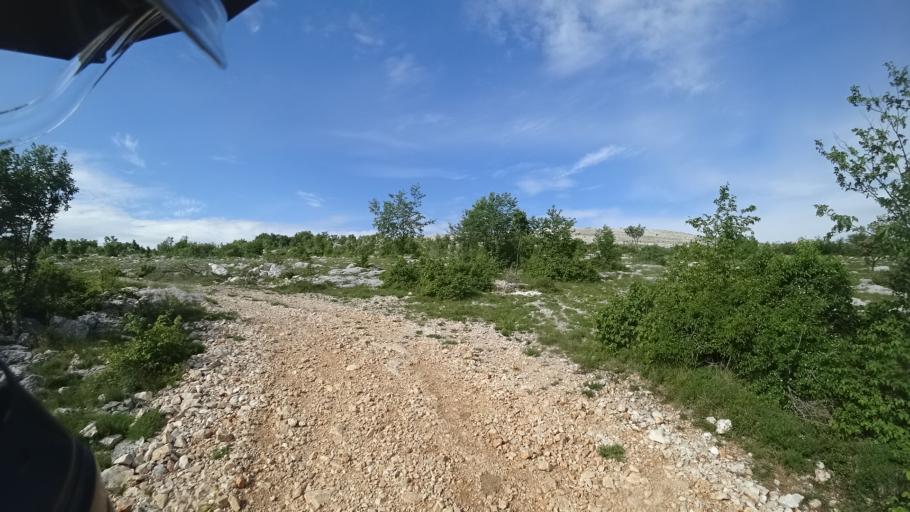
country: HR
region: Splitsko-Dalmatinska
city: Hrvace
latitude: 43.7845
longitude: 16.4373
